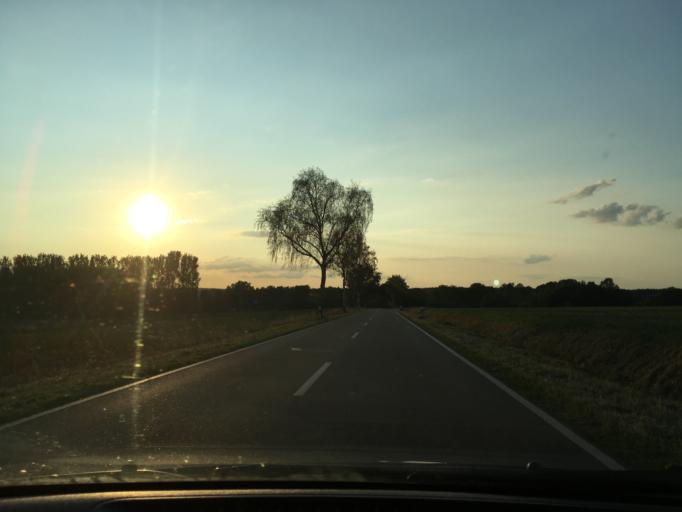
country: DE
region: Lower Saxony
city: Bleckede
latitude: 53.2580
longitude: 10.7537
